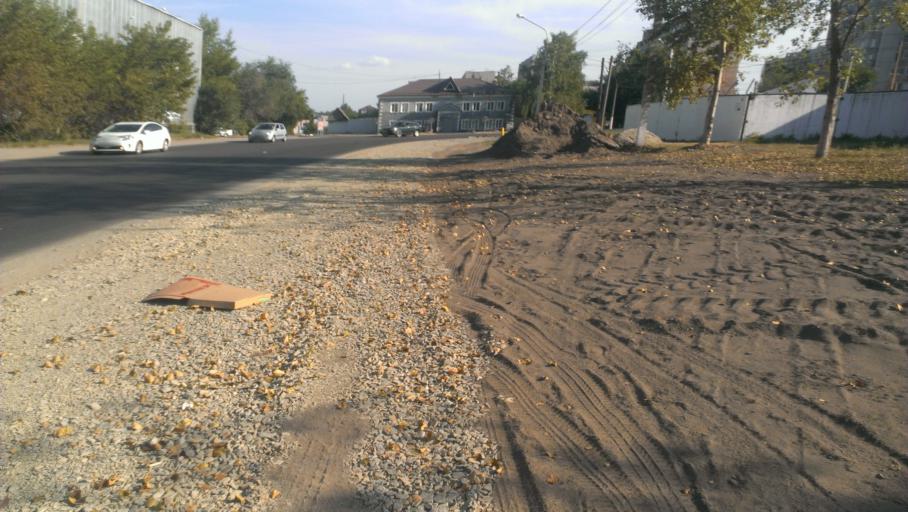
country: RU
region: Altai Krai
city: Novosilikatnyy
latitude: 53.3091
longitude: 83.6222
